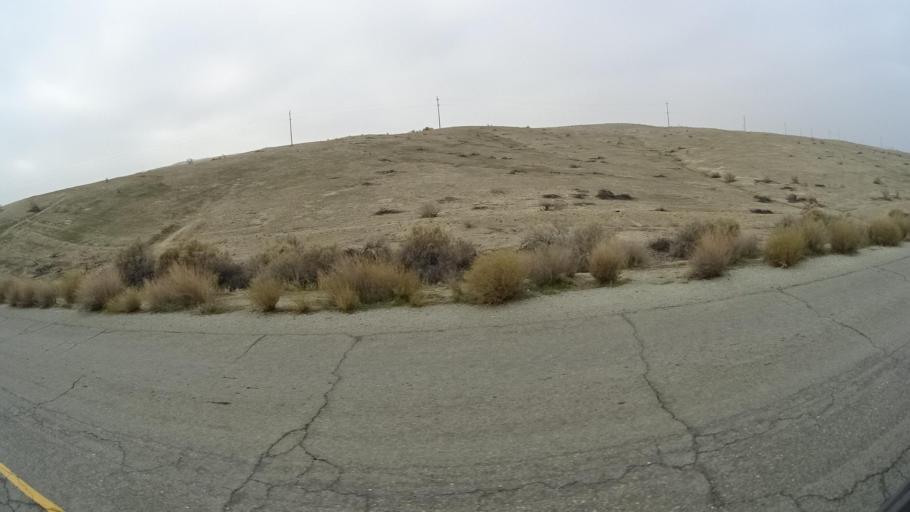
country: US
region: California
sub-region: Kern County
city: Maricopa
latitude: 35.1464
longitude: -119.3394
